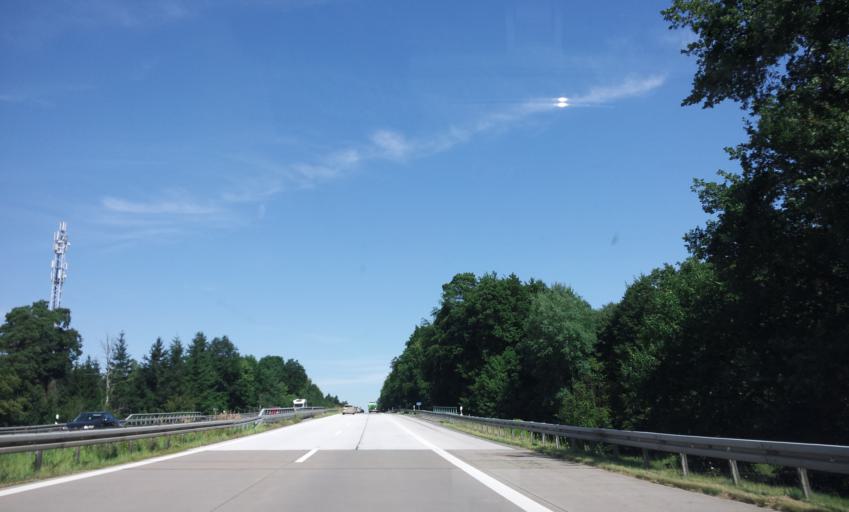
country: DE
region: Brandenburg
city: Althuttendorf
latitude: 53.0203
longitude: 13.8282
